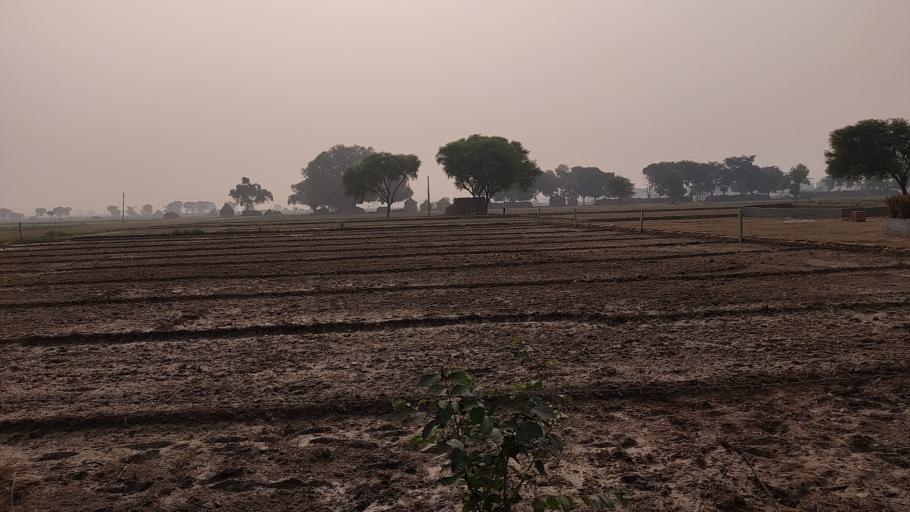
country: IN
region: Uttar Pradesh
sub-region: Mathura
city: Vrindavan
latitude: 27.5535
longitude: 77.7144
